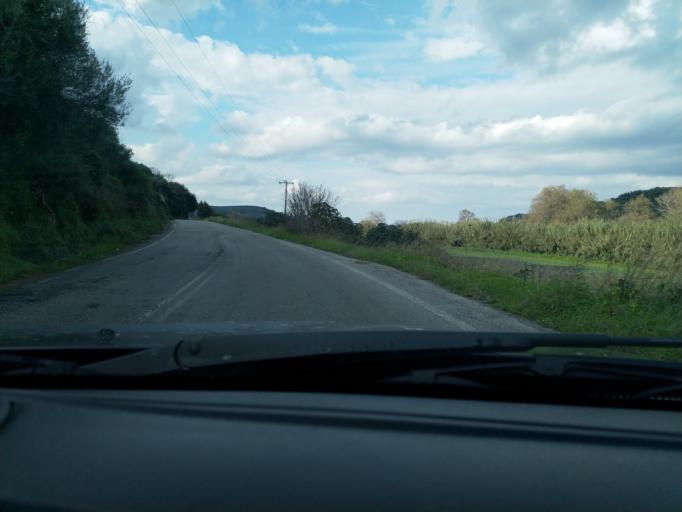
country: GR
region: Crete
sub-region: Nomos Chanias
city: Agia Marina
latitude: 35.4960
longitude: 23.9058
